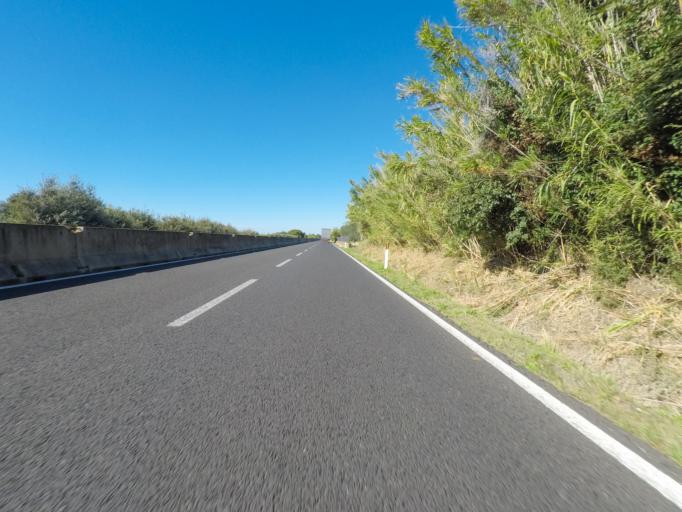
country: IT
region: Tuscany
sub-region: Provincia di Grosseto
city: Orbetello Scalo
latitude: 42.4595
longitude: 11.2468
